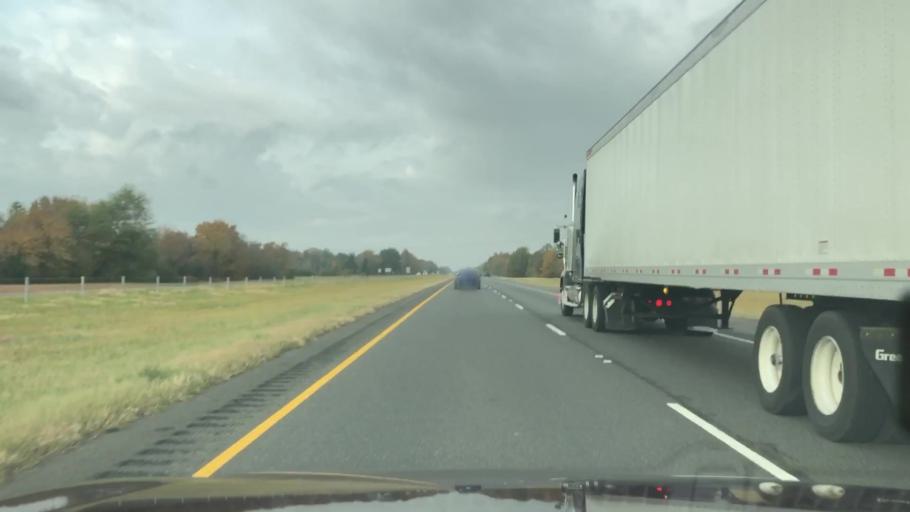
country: US
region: Louisiana
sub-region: Richland Parish
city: Delhi
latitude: 32.4514
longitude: -91.5822
